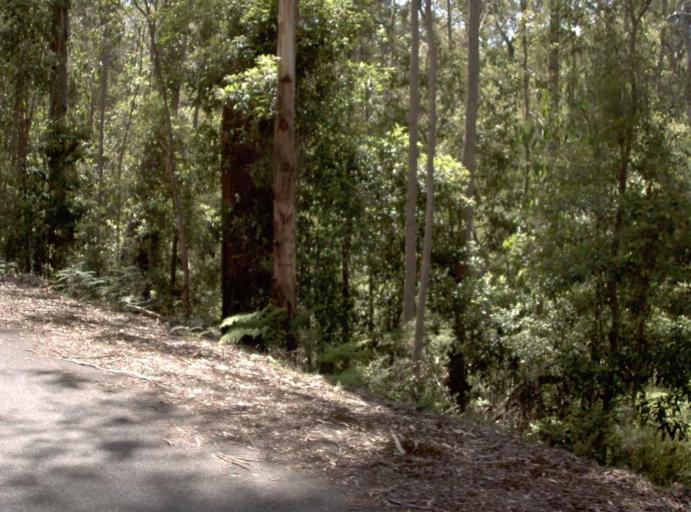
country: AU
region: New South Wales
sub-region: Bombala
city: Bombala
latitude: -37.5064
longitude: 148.9275
